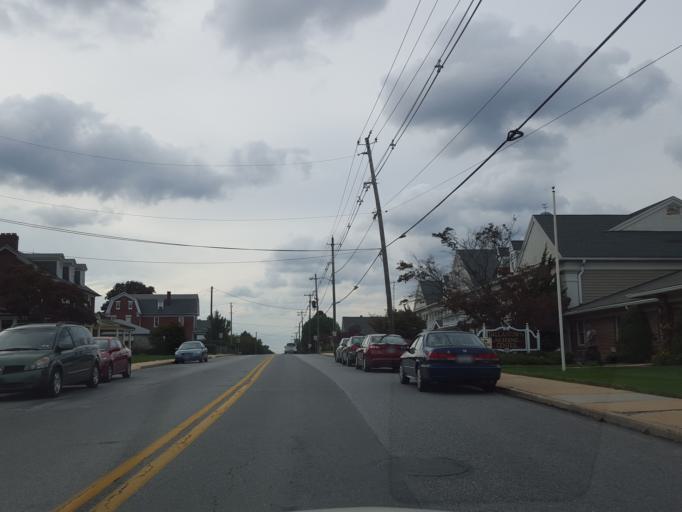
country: US
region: Pennsylvania
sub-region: York County
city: Dallastown
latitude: 39.8987
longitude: -76.6280
